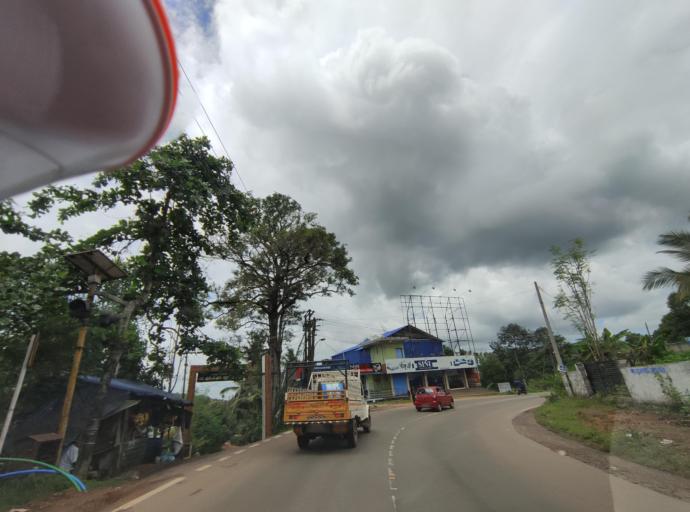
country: IN
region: Kerala
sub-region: Thiruvananthapuram
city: Nedumangad
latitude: 8.5823
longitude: 76.9479
